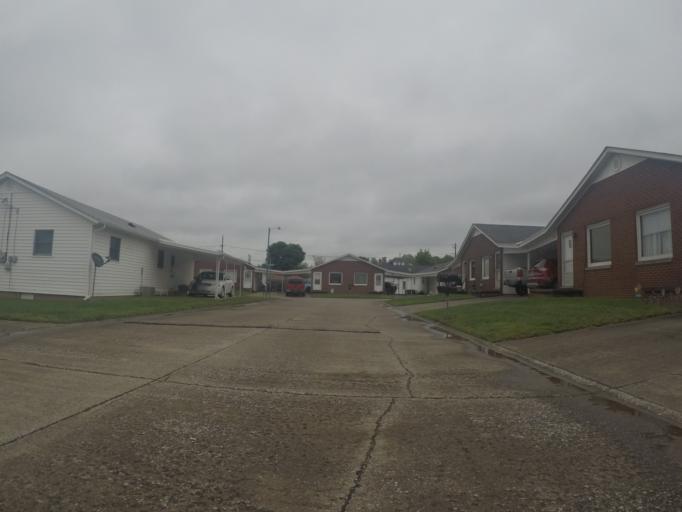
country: US
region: West Virginia
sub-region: Cabell County
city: Barboursville
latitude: 38.4129
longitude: -82.3000
